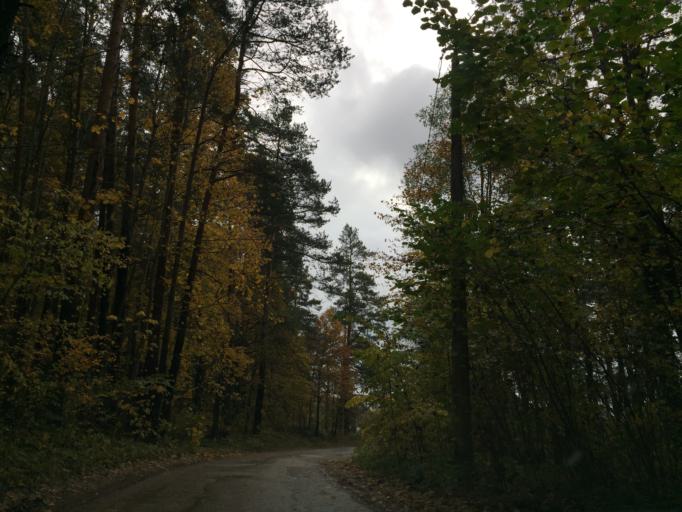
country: LV
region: Ogre
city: Ogre
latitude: 56.7973
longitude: 24.6400
